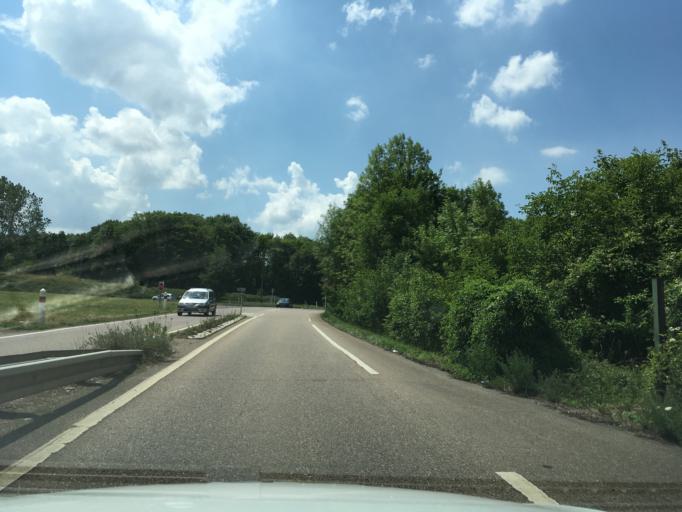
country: FR
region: Lorraine
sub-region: Departement de la Moselle
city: Saint-Julien-les-Metz
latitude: 49.1201
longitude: 6.2232
